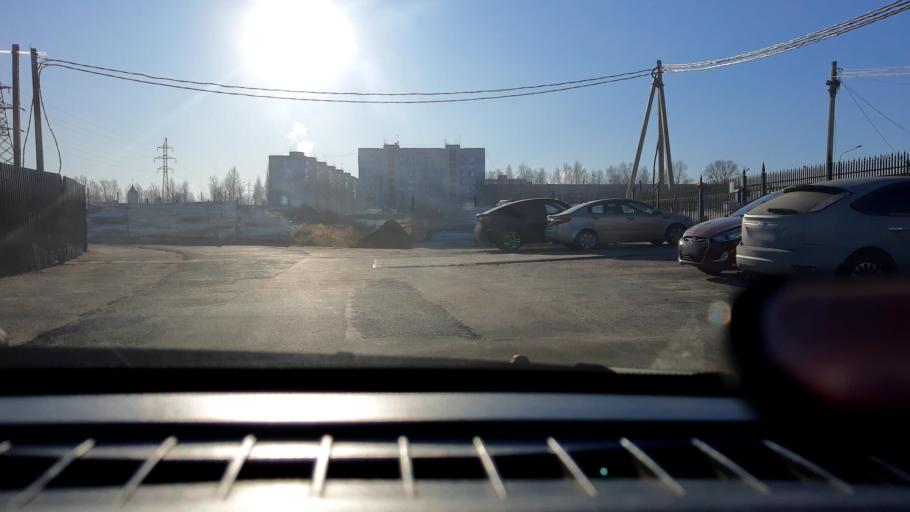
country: RU
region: Nizjnij Novgorod
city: Gorbatovka
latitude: 56.3838
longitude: 43.7988
